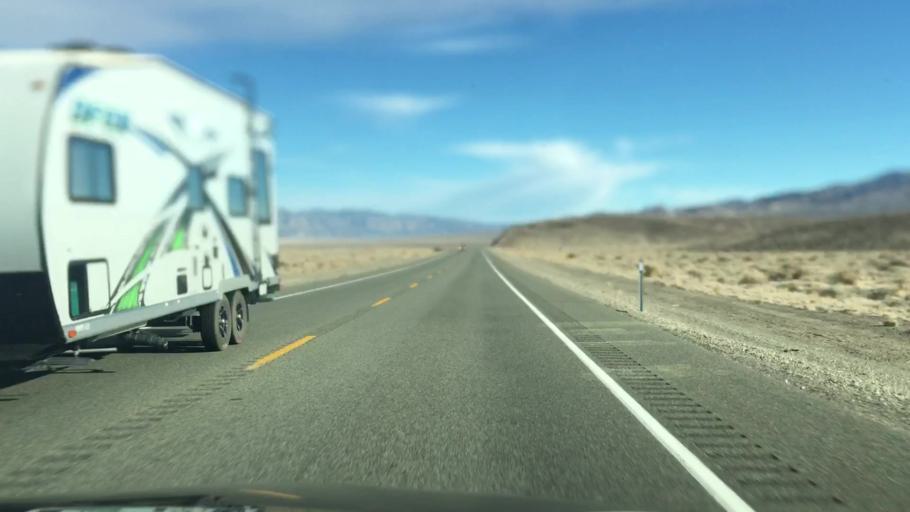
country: US
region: Nevada
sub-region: Mineral County
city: Hawthorne
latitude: 38.5464
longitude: -118.4157
